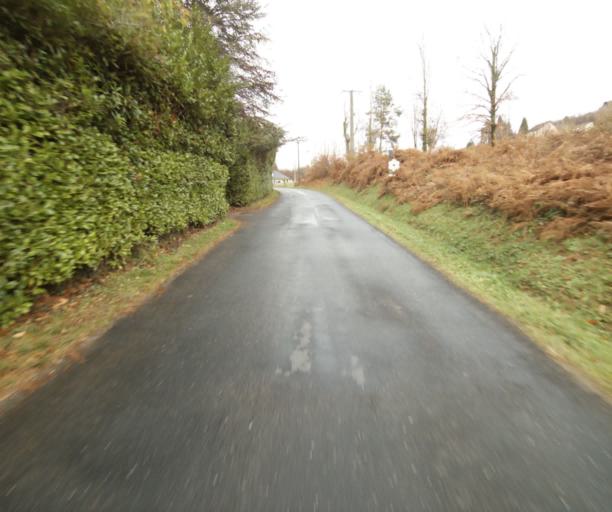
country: FR
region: Limousin
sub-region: Departement de la Correze
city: Saint-Mexant
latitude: 45.2799
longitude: 1.6404
